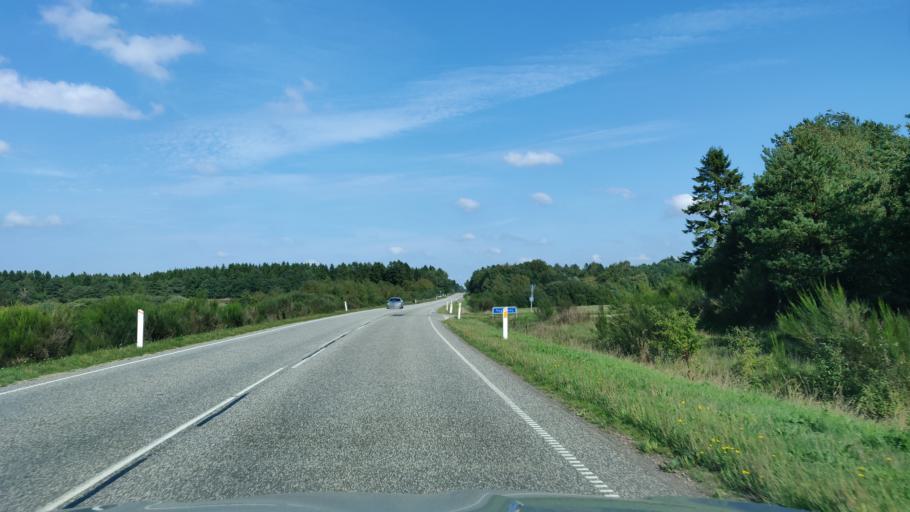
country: DK
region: Central Jutland
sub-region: Herning Kommune
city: Sunds
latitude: 56.3566
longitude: 8.9730
